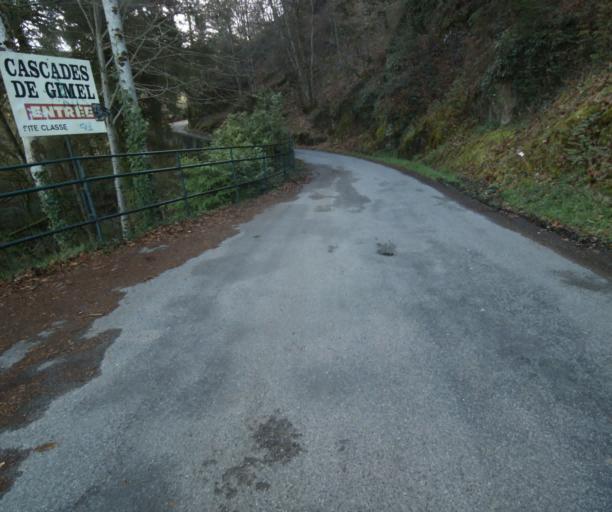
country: FR
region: Limousin
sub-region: Departement de la Correze
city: Correze
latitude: 45.2978
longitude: 1.8484
